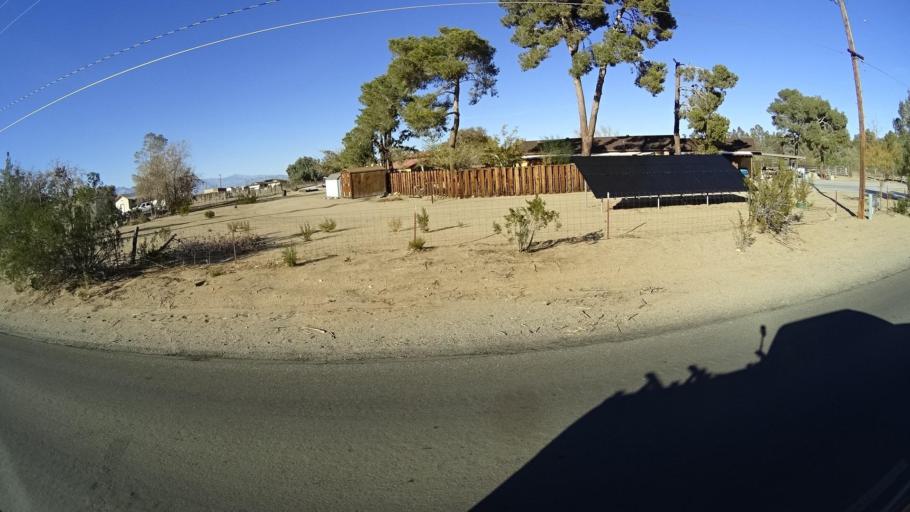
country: US
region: California
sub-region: Kern County
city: Ridgecrest
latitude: 35.6372
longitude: -117.7109
